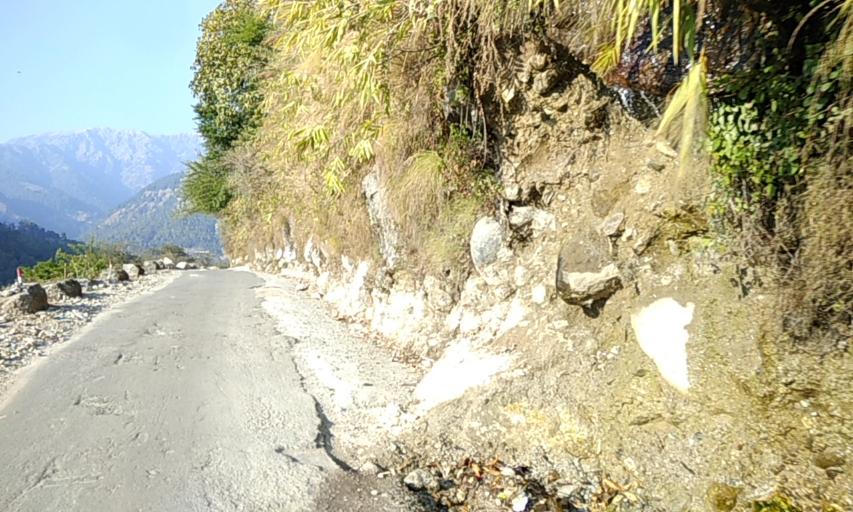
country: IN
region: Himachal Pradesh
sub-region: Kangra
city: Palampur
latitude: 32.1337
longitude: 76.5352
